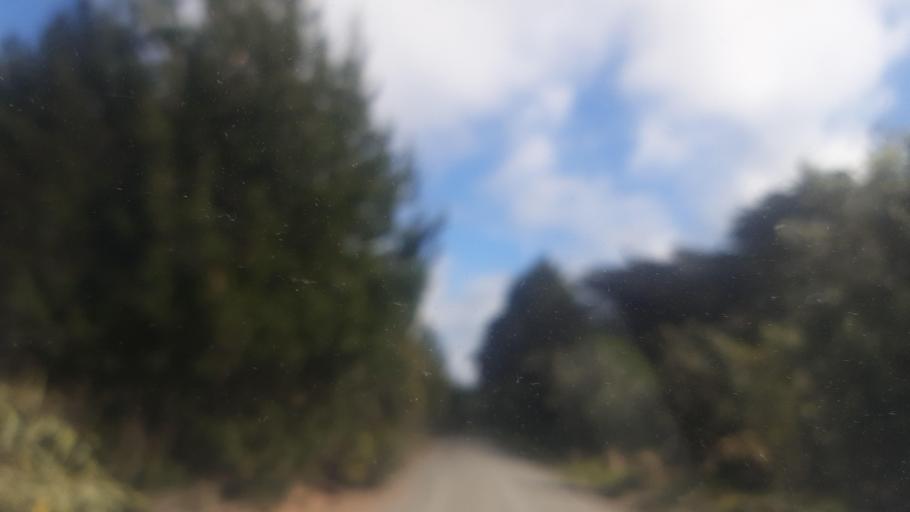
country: NZ
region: Northland
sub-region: Far North District
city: Kaitaia
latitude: -34.7661
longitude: 173.0450
